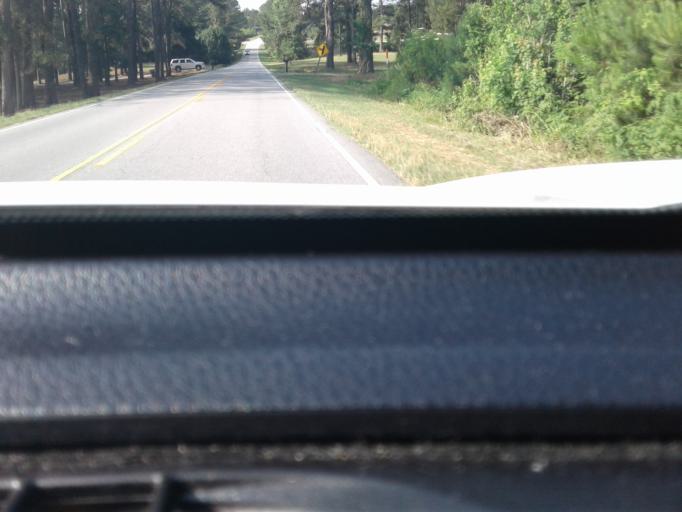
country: US
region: North Carolina
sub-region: Johnston County
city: Benson
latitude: 35.4094
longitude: -78.5404
